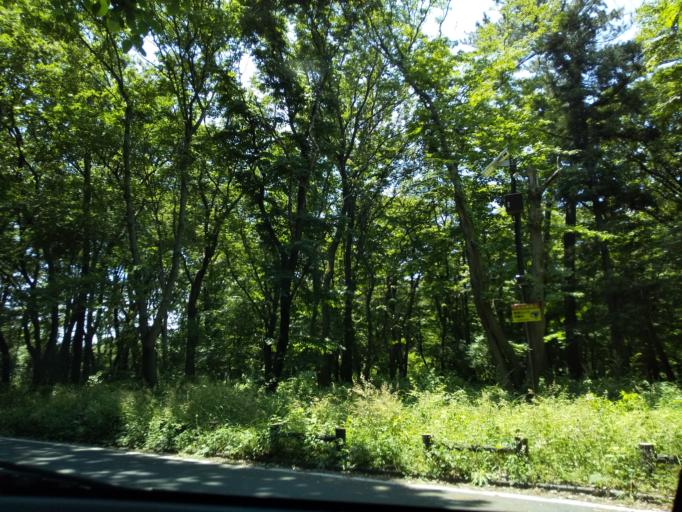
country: JP
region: Tokyo
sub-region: Machida-shi
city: Machida
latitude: 35.5412
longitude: 139.4090
